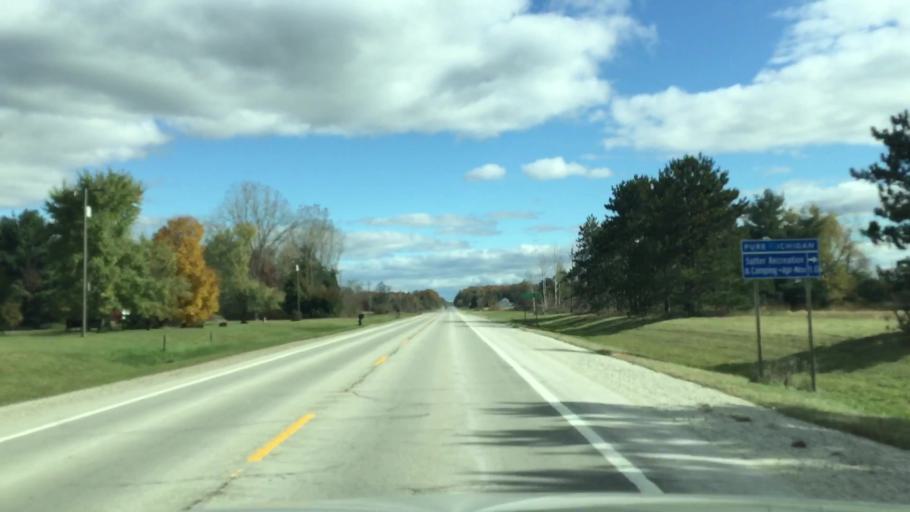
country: US
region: Michigan
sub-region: Lapeer County
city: Barnes Lake-Millers Lake
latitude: 43.2272
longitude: -83.2881
